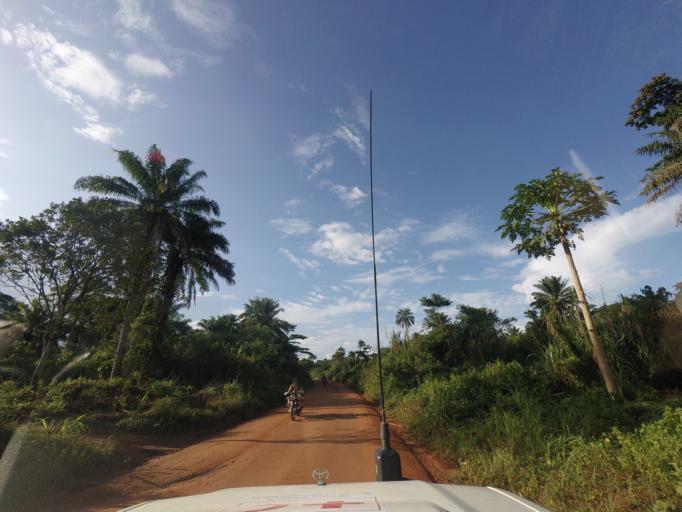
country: GN
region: Nzerekore
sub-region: Nzerekore Prefecture
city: Nzerekore
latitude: 7.7020
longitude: -8.8195
